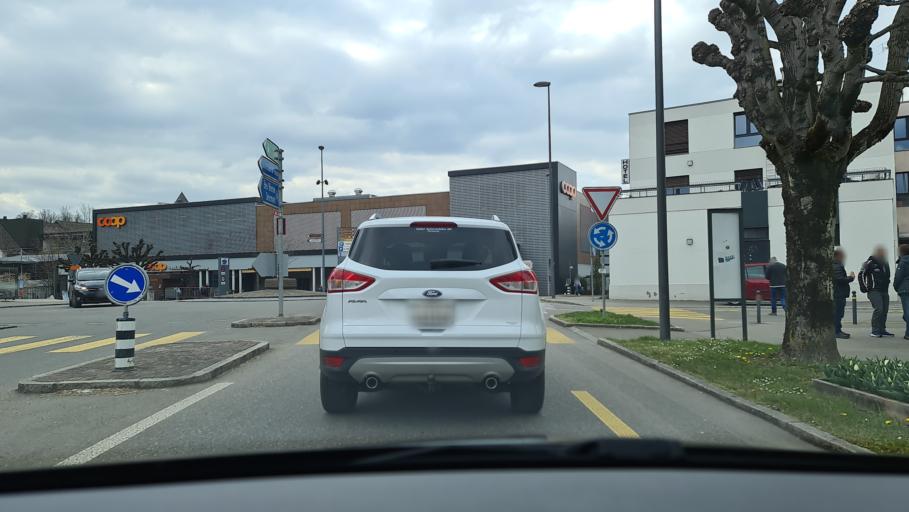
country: CH
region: Jura
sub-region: Porrentruy District
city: Porrentruy
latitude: 47.4165
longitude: 7.0786
